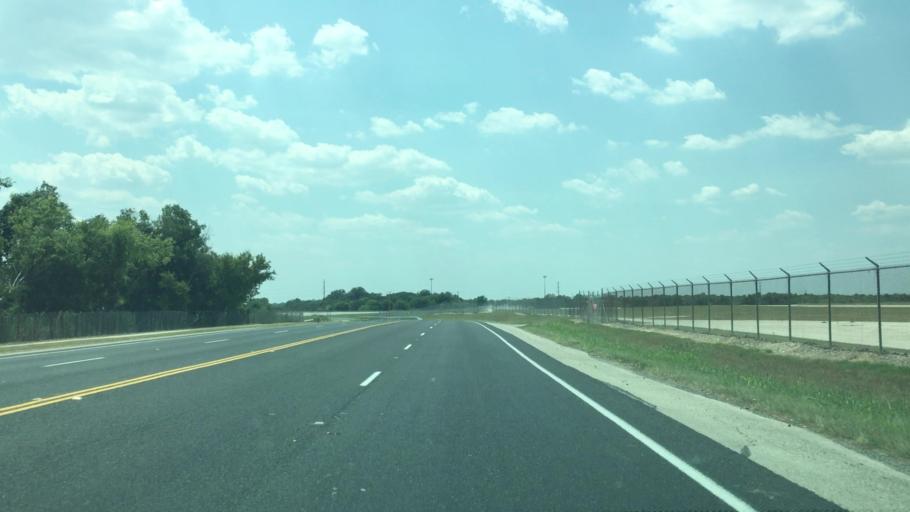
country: US
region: Texas
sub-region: Travis County
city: Austin
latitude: 30.1752
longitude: -97.6761
